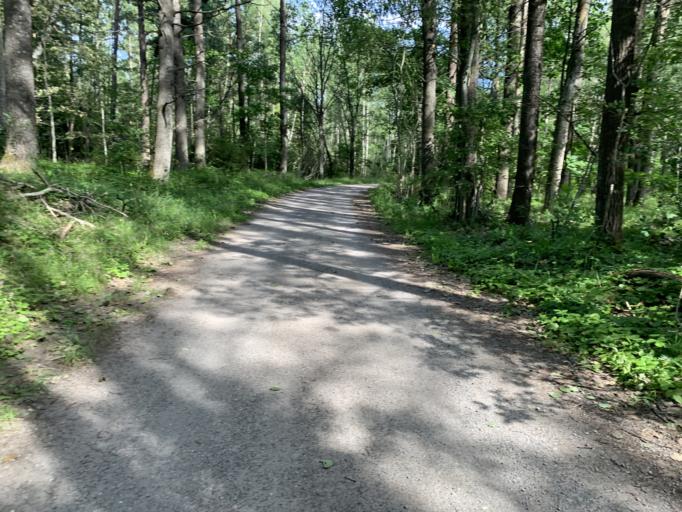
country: SE
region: Stockholm
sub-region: Stockholms Kommun
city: Kista
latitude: 59.3980
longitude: 17.9682
